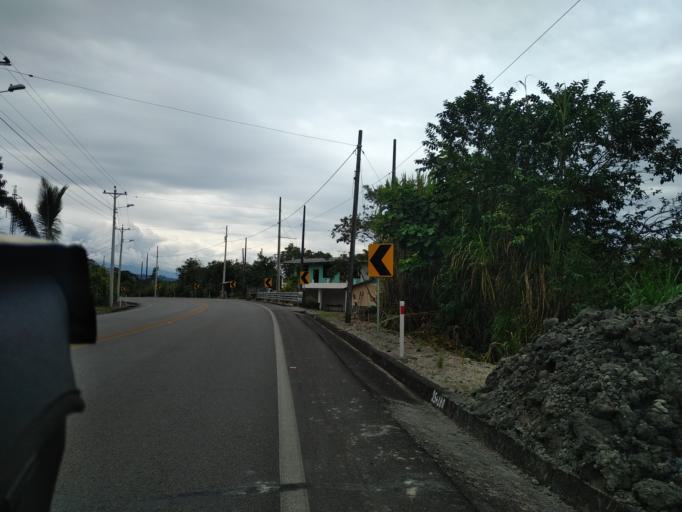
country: EC
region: Napo
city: Tena
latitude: -1.2005
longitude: -77.8737
